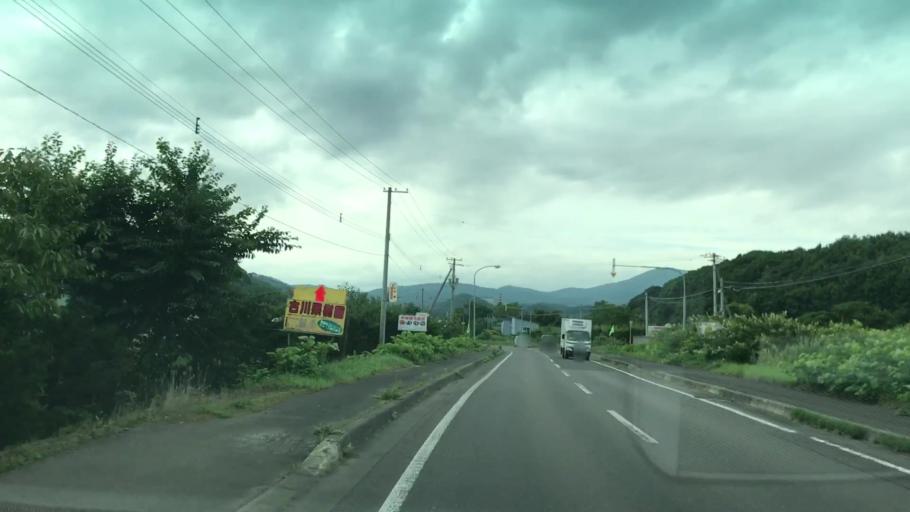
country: JP
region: Hokkaido
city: Yoichi
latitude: 43.1751
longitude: 140.8219
